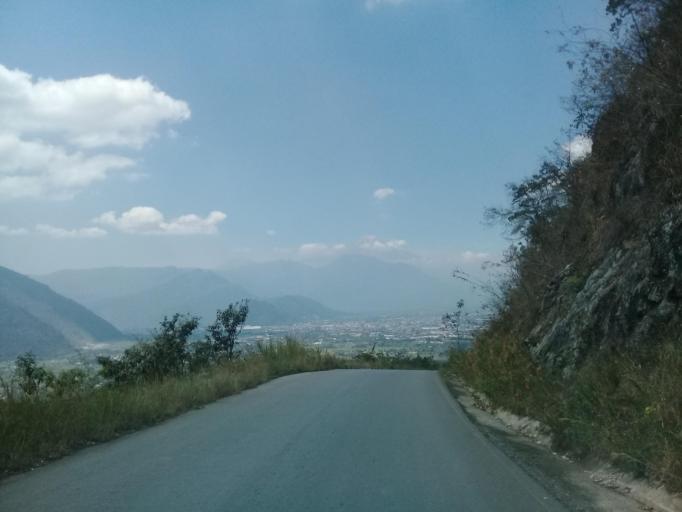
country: MX
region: Veracruz
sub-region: Tlilapan
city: Tonalixco
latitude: 18.8035
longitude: -97.0592
